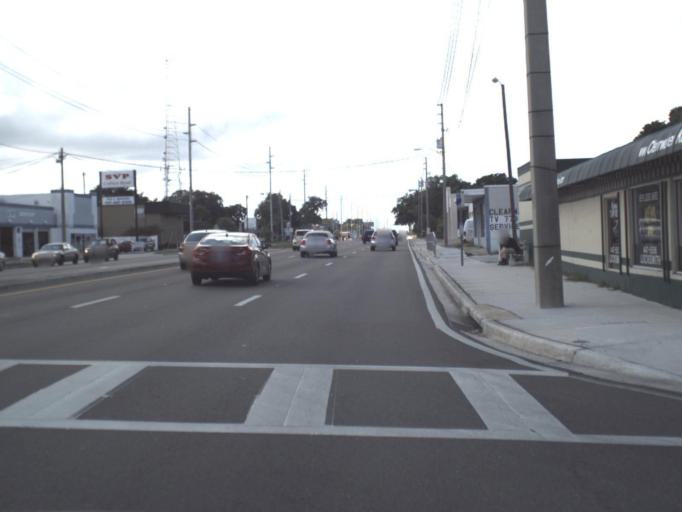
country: US
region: Florida
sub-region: Pinellas County
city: Clearwater
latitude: 27.9498
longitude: -82.7876
